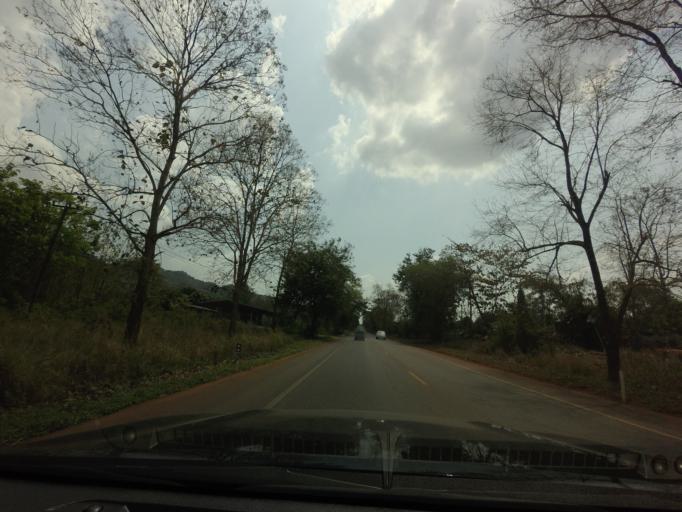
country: TH
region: Kanchanaburi
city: Sai Yok
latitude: 14.1606
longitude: 99.1370
